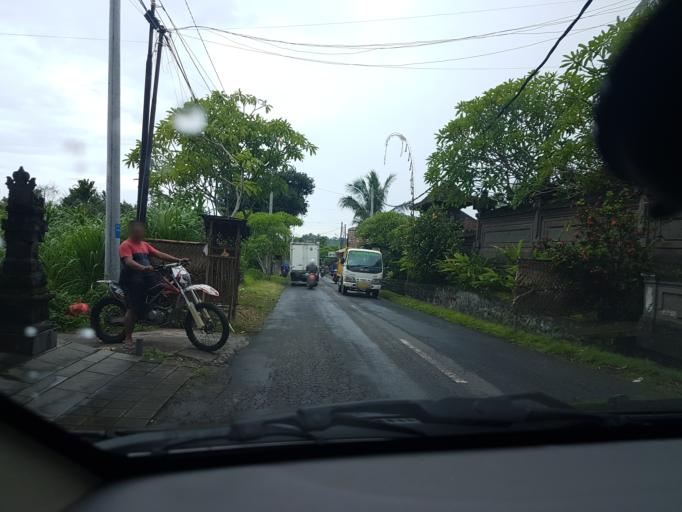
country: ID
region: Bali
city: Banjar Tebongkang
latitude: -8.5225
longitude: 115.2392
